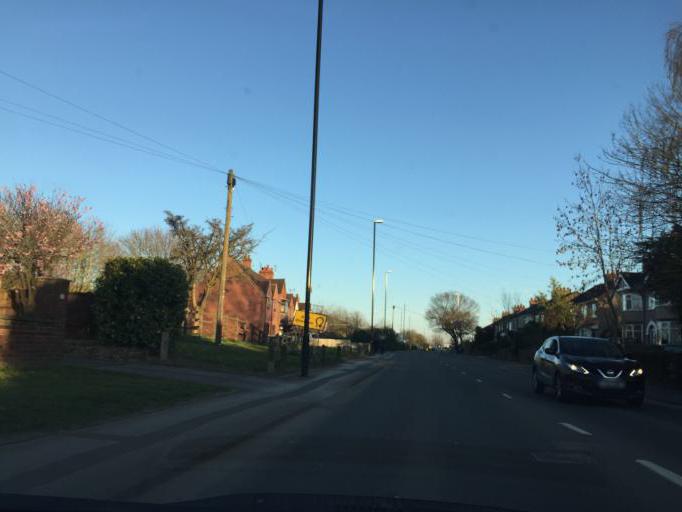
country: GB
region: England
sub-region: Warwickshire
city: Ryton on Dunsmore
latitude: 52.4009
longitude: -1.4444
